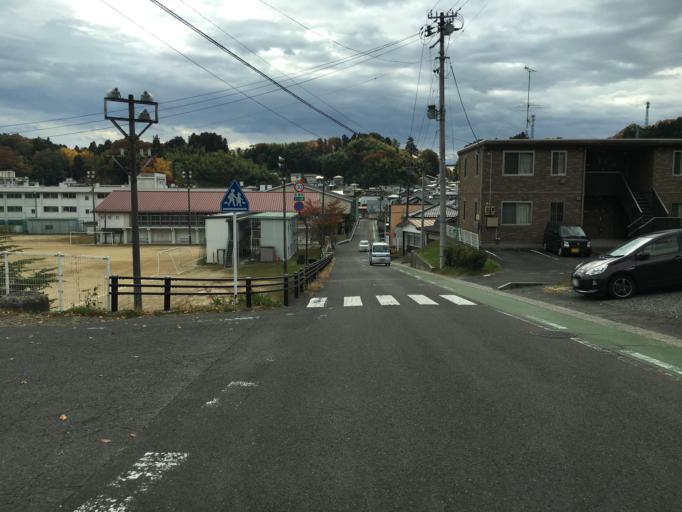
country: JP
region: Fukushima
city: Nihommatsu
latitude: 37.6014
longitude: 140.4395
